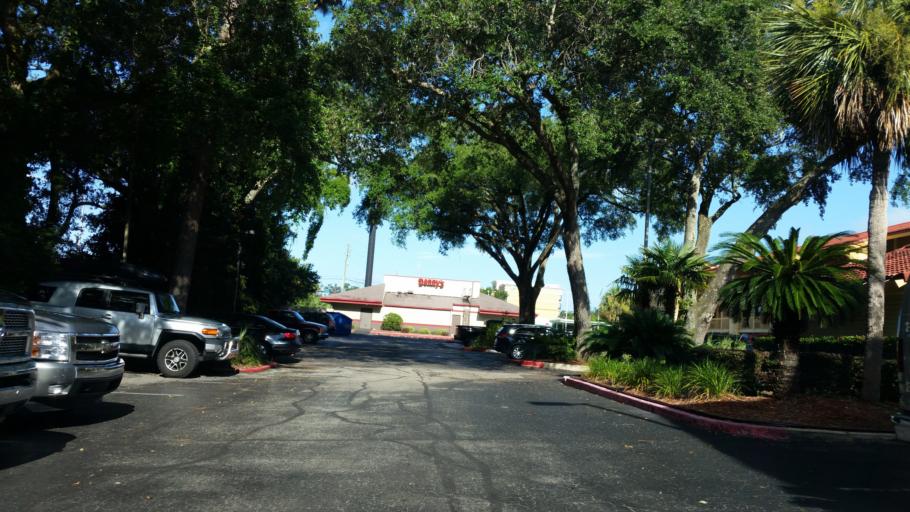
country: US
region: Florida
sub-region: Escambia County
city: Ferry Pass
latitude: 30.5057
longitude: -87.2198
